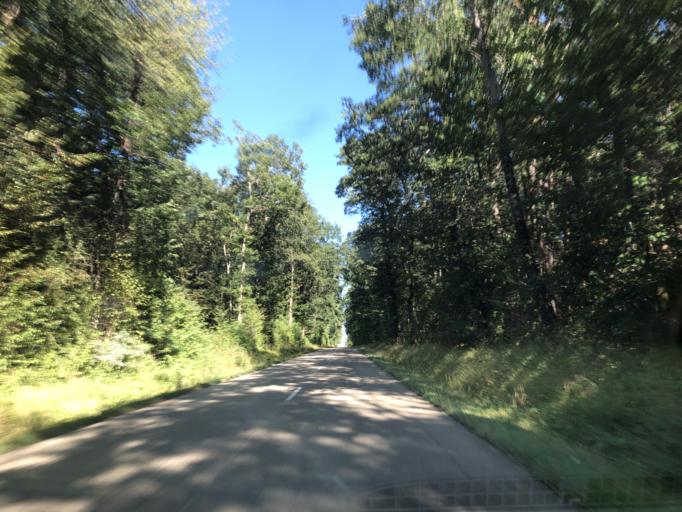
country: FR
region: Bourgogne
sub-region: Departement de l'Yonne
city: Gurgy
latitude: 47.8994
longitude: 3.5691
